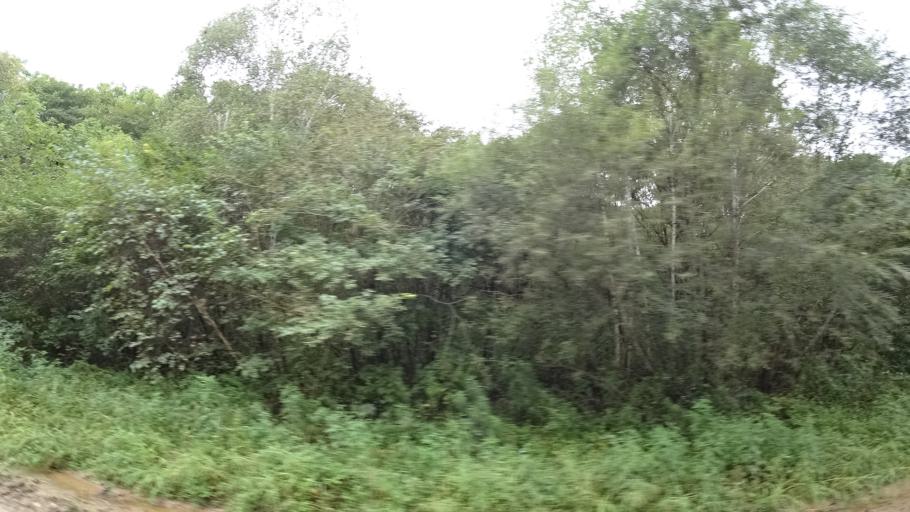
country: RU
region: Primorskiy
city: Rettikhovka
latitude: 44.0598
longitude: 132.6543
